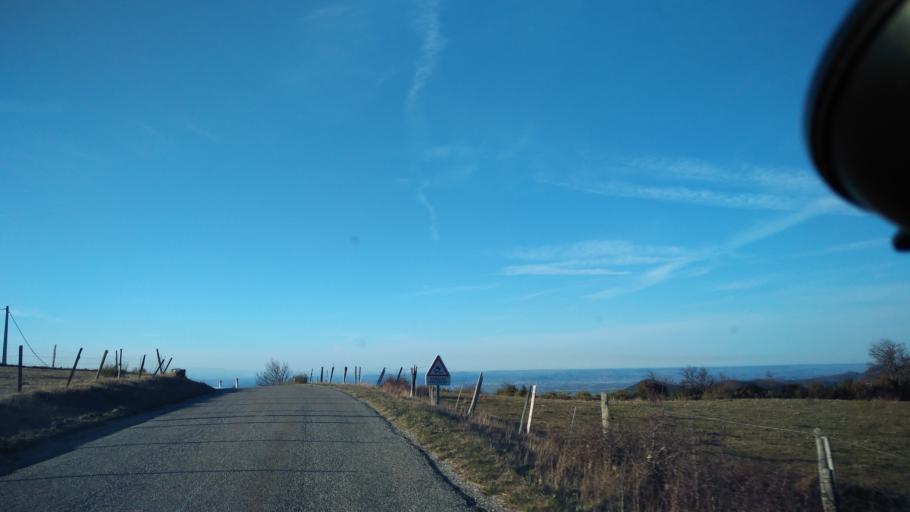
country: FR
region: Rhone-Alpes
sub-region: Departement de la Drome
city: Chabeuil
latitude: 44.8485
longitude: 5.0924
